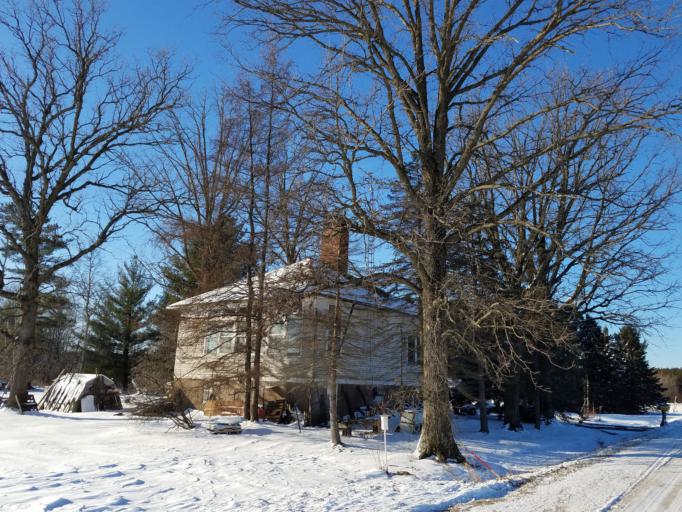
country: US
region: Wisconsin
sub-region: Clark County
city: Loyal
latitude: 44.6613
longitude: -90.4163
